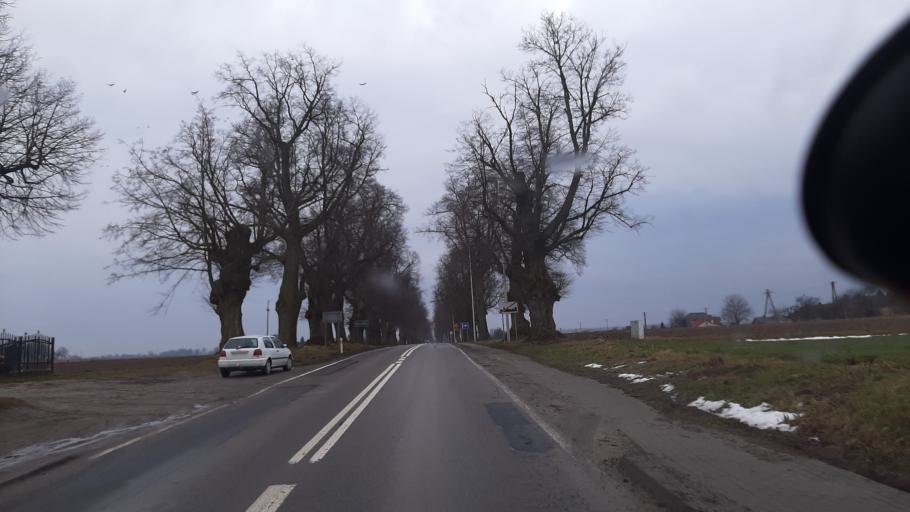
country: PL
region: Lublin Voivodeship
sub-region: Powiat lubelski
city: Jastkow
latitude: 51.3594
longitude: 22.4694
